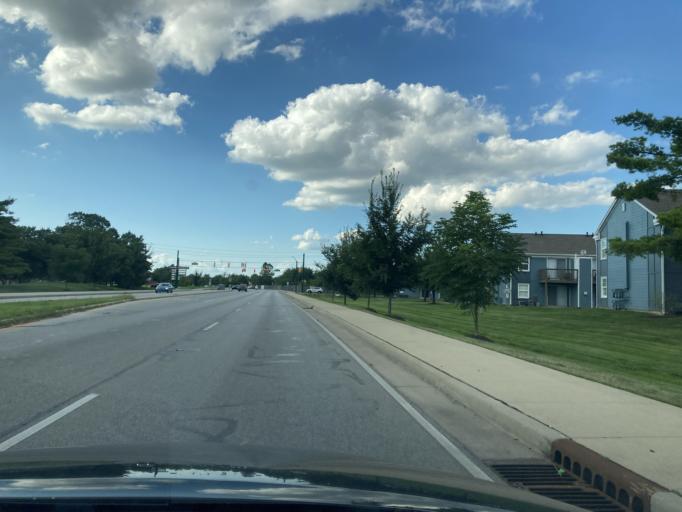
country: US
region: Indiana
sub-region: Marion County
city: Speedway
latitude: 39.8592
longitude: -86.2407
